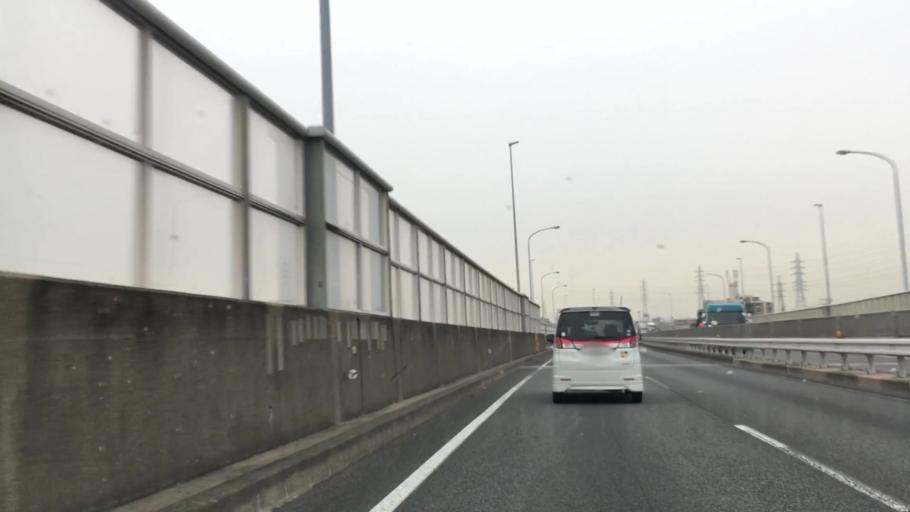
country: JP
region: Aichi
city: Chiryu
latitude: 35.0089
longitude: 137.0258
